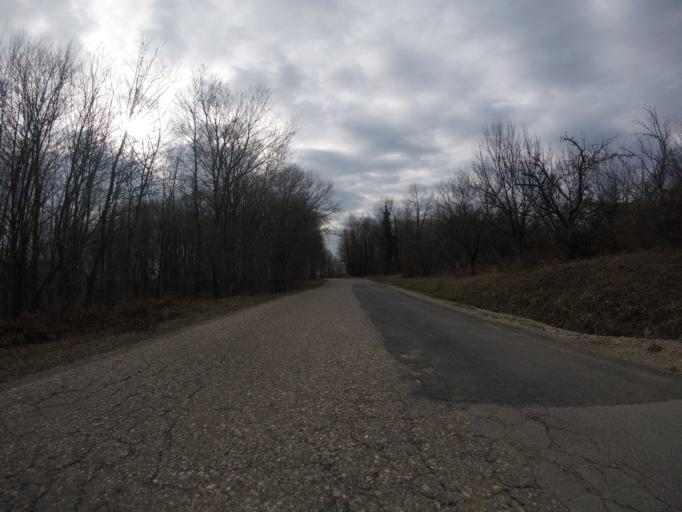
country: HR
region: Zagrebacka
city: Mraclin
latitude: 45.5286
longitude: 16.0524
